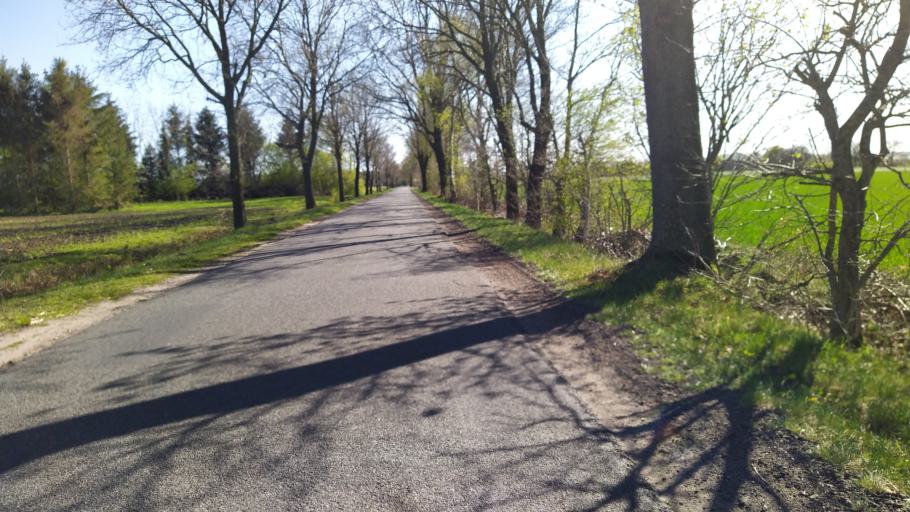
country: DE
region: Lower Saxony
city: Heeslingen
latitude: 53.3121
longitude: 9.3864
